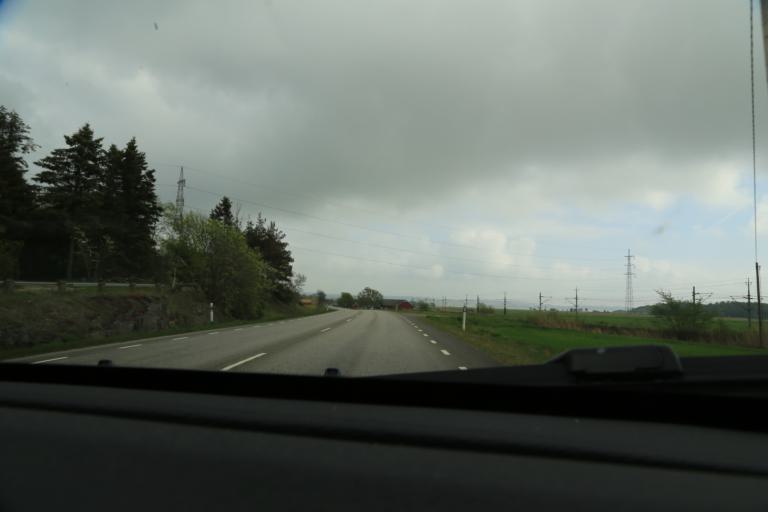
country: SE
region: Halland
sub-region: Kungsbacka Kommun
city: Frillesas
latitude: 57.2382
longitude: 12.1987
